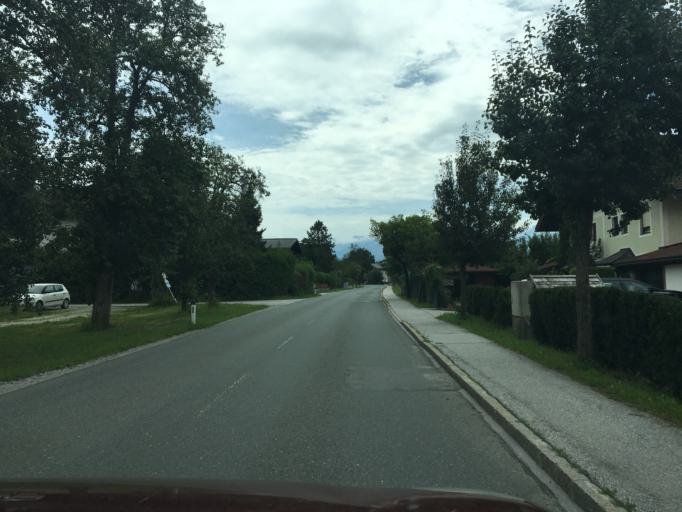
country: AT
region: Salzburg
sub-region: Politischer Bezirk Hallein
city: Adnet
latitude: 47.6630
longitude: 13.1394
